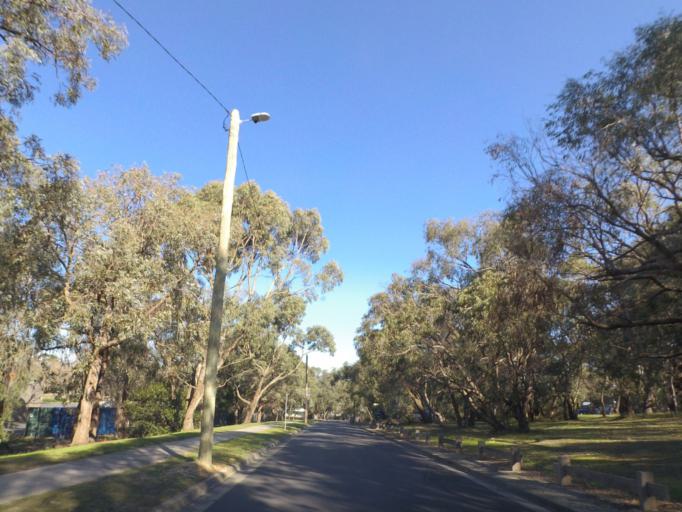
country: AU
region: Victoria
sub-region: Maroondah
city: Ringwood East
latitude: -37.8228
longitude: 145.2313
